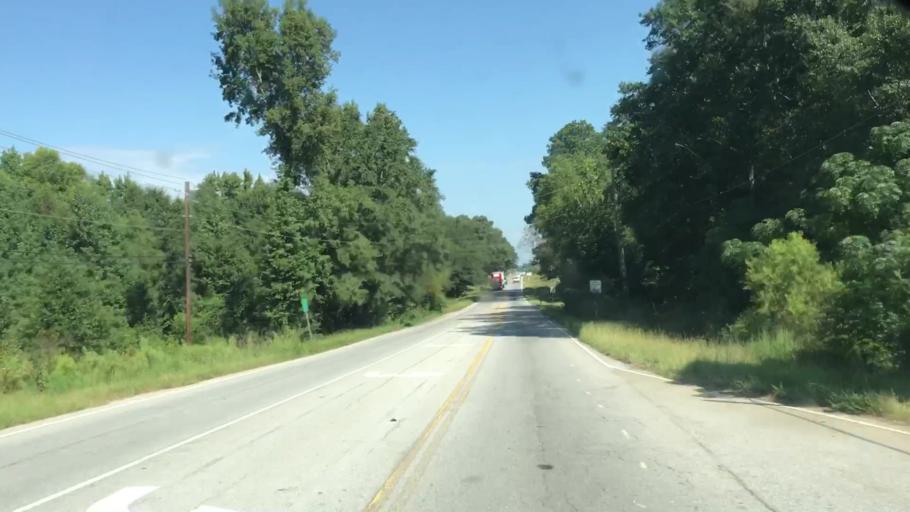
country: US
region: Georgia
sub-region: Walton County
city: Loganville
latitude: 33.8491
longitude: -83.9019
